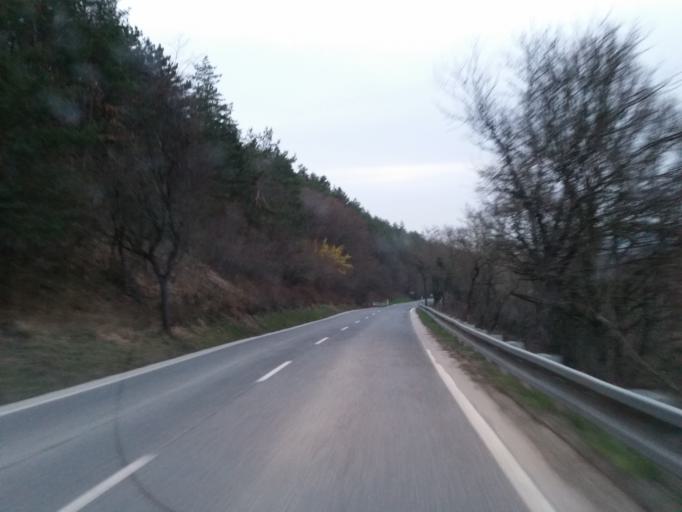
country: SK
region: Trnavsky
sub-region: Okres Trnava
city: Piestany
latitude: 48.5741
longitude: 17.8514
